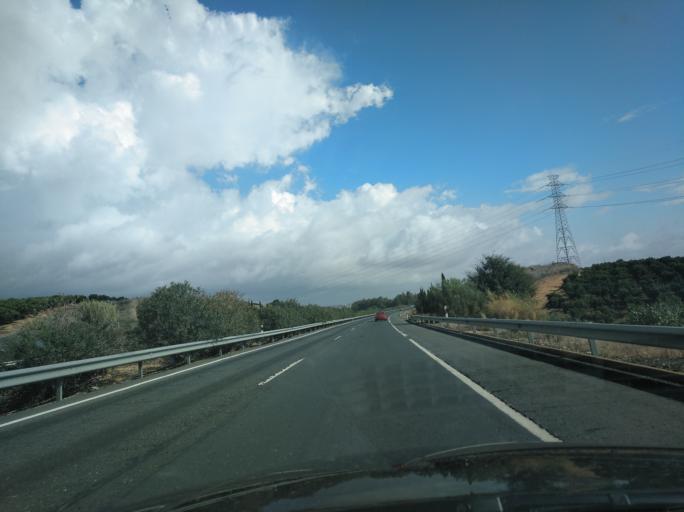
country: ES
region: Andalusia
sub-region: Provincia de Huelva
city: Gibraleon
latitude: 37.3461
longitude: -6.9965
